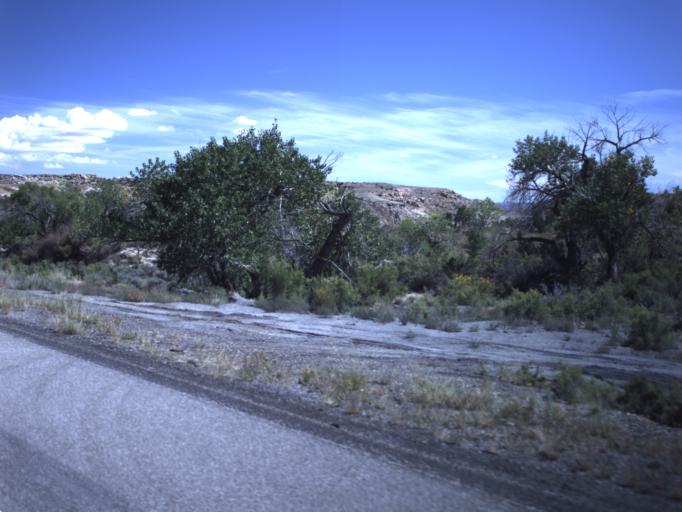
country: US
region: Utah
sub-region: Emery County
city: Ferron
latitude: 38.8133
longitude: -111.1995
